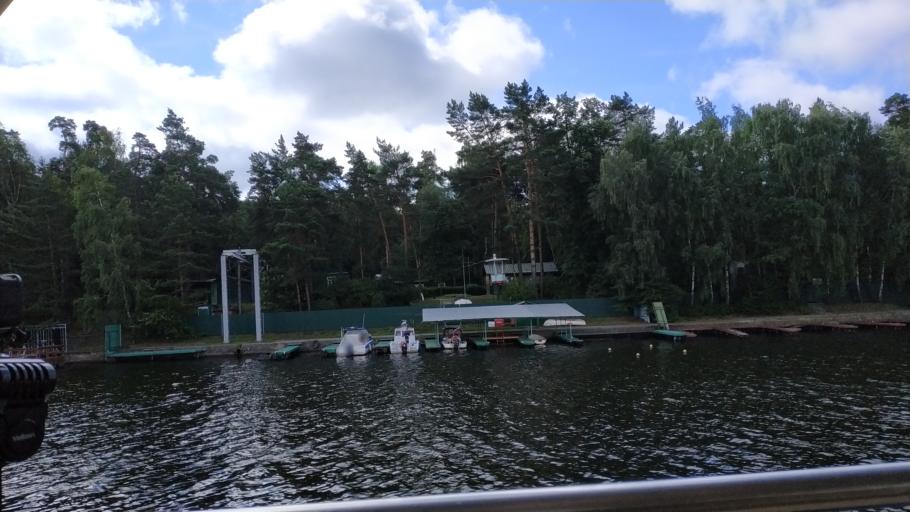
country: RU
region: Moscow
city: Shchukino
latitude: 55.7866
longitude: 37.4334
